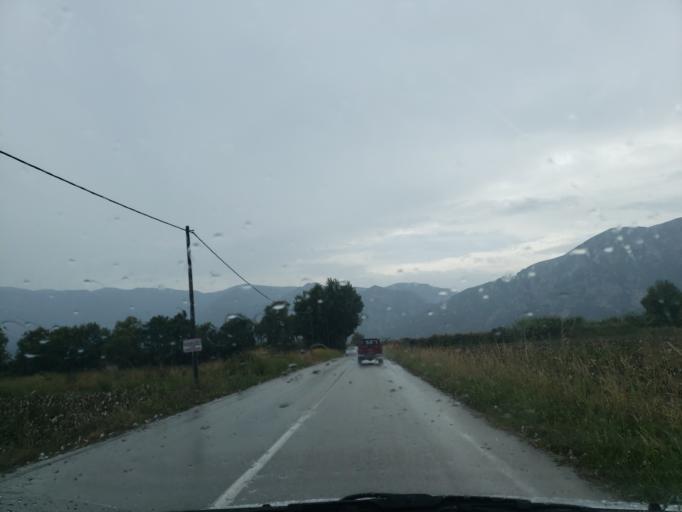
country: GR
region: Central Greece
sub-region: Nomos Fthiotidos
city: Anthili
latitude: 38.8194
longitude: 22.4420
